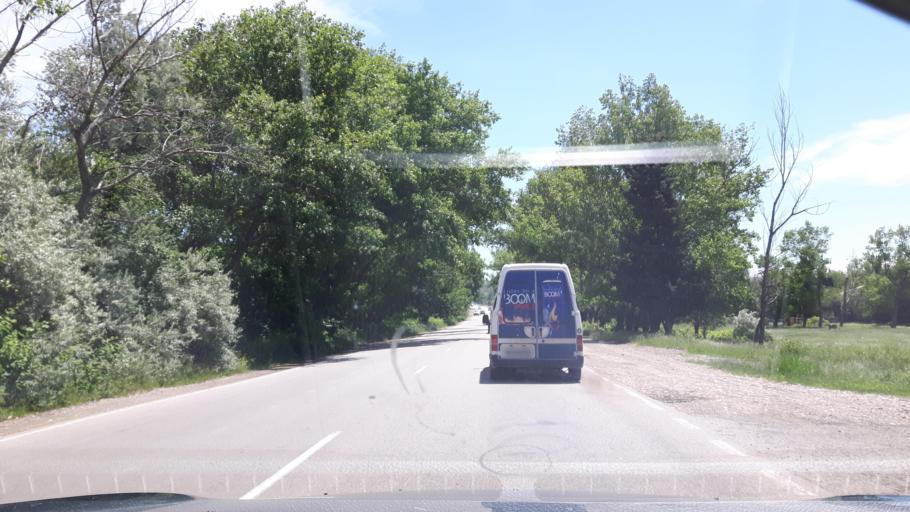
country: GE
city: Didi Lilo
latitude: 41.6946
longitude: 45.0589
